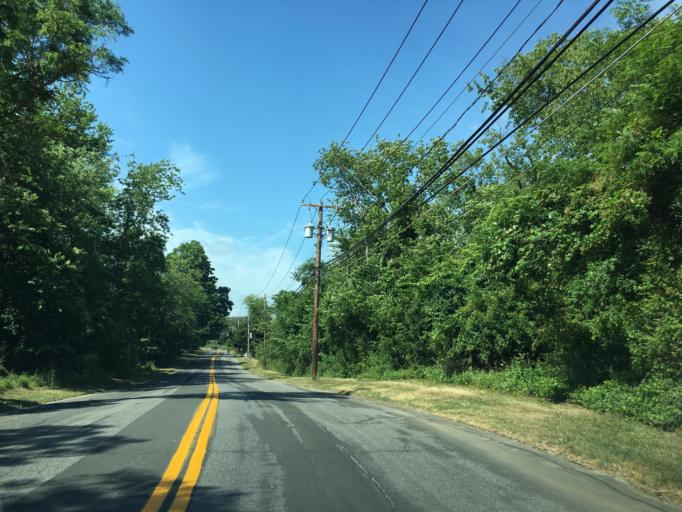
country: US
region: New York
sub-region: Suffolk County
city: Shelter Island Heights
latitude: 41.0591
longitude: -72.3681
